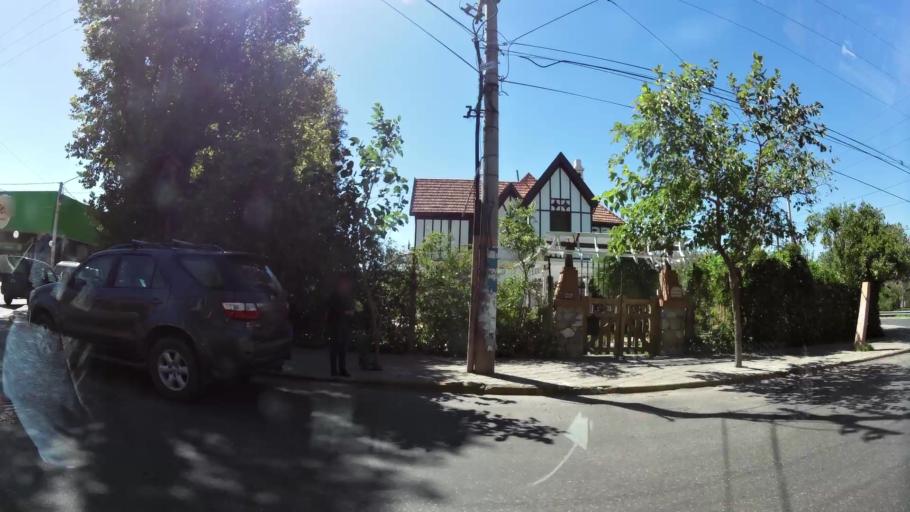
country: AR
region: San Juan
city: Villa Krause
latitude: -31.5543
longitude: -68.5226
